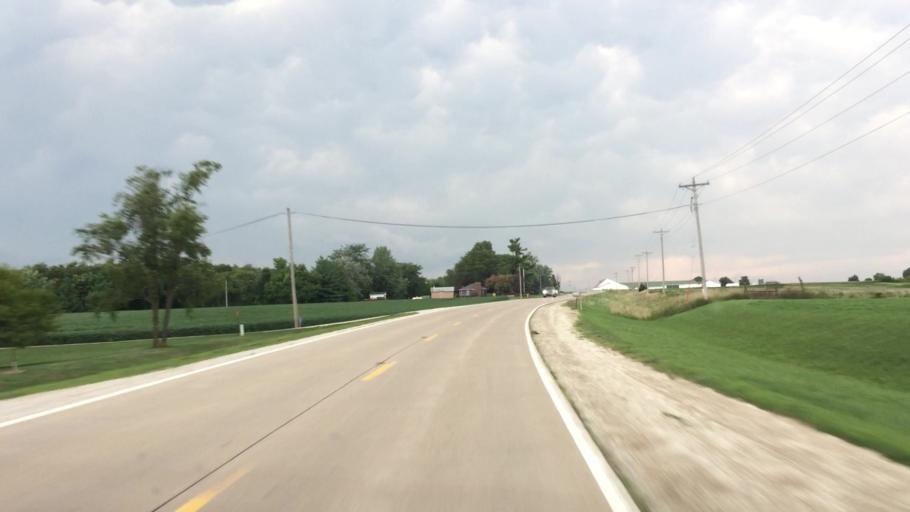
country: US
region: Iowa
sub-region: Lee County
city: Fort Madison
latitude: 40.7320
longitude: -91.3295
